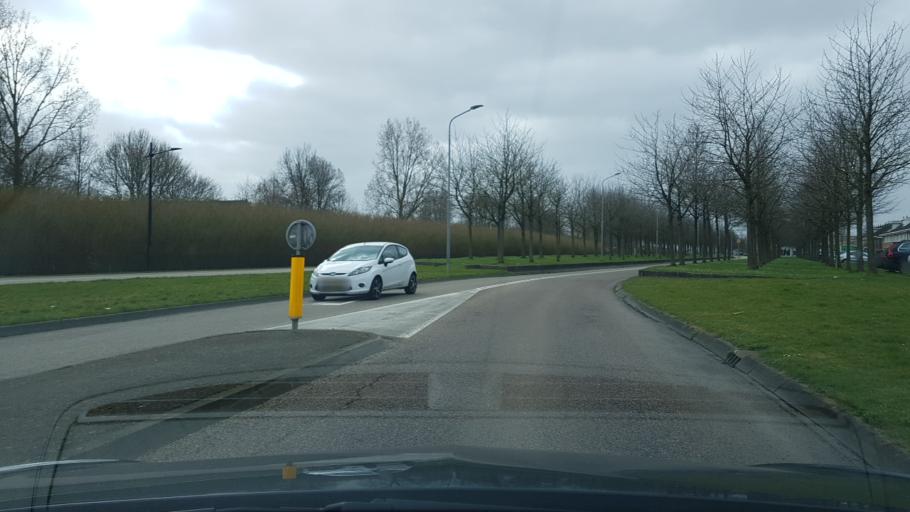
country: NL
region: South Holland
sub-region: Gemeente Hillegom
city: Hillegom
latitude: 52.2667
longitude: 4.6159
